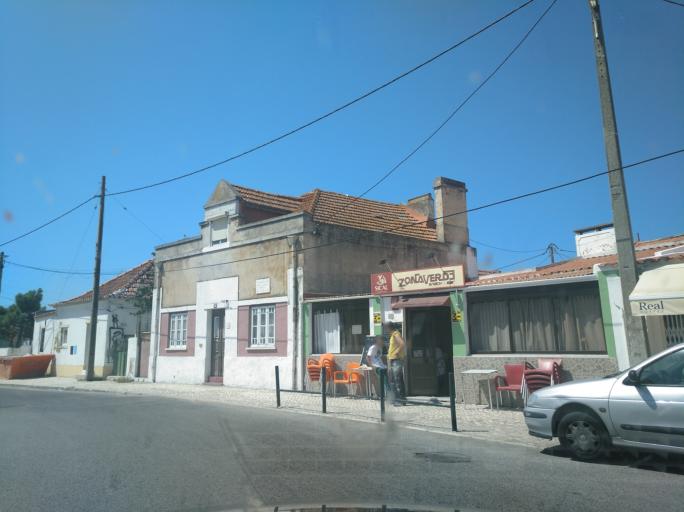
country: PT
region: Setubal
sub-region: Almada
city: Trafaria
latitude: 38.6709
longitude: -9.2367
